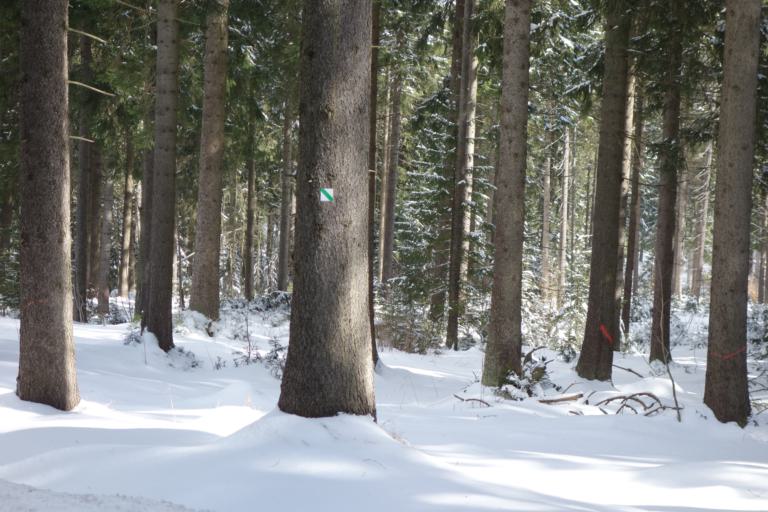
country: DE
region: Saxony
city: Eibenstock
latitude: 50.4380
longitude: 12.6064
